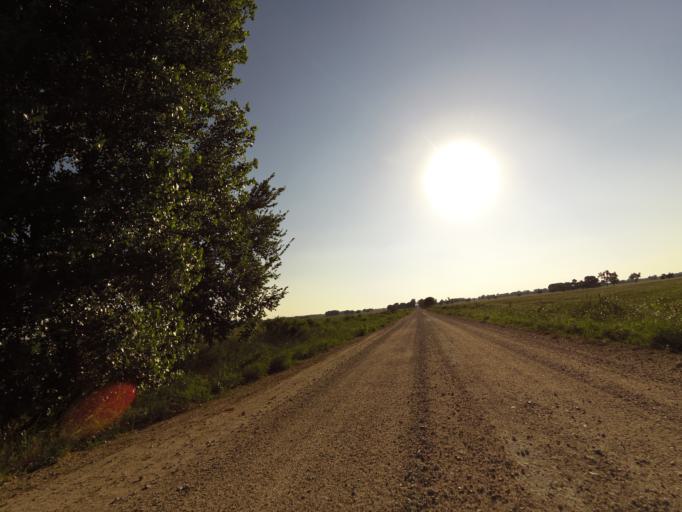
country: US
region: Kansas
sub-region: McPherson County
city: Inman
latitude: 38.1883
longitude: -97.8694
